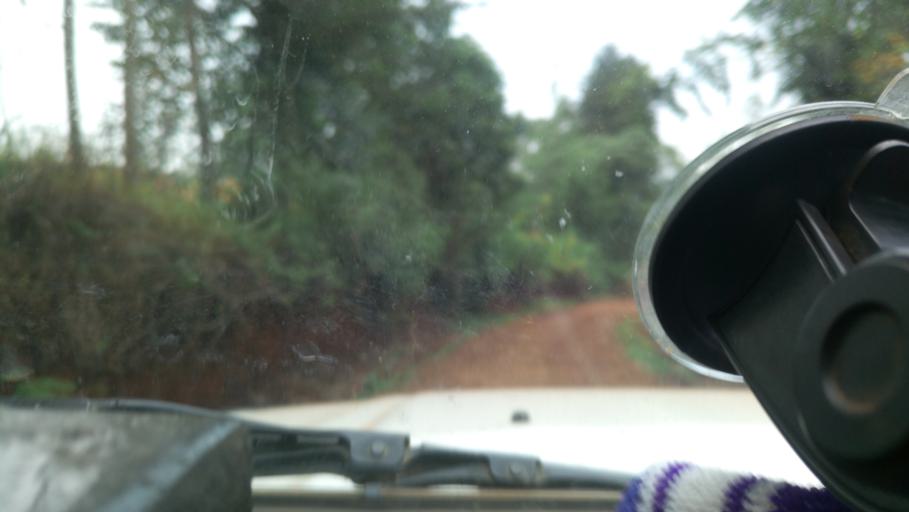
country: KE
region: Kericho
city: Sotik
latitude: -0.6580
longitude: 35.1516
